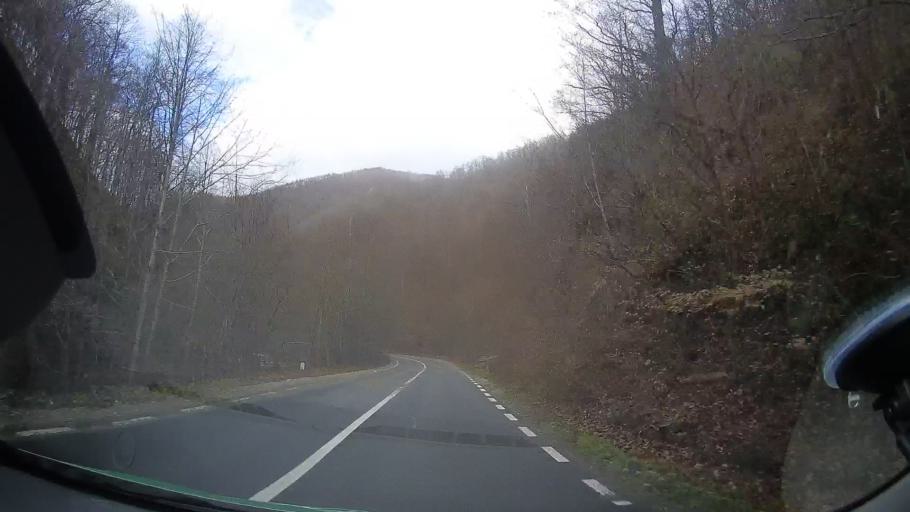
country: RO
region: Cluj
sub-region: Comuna Valea Ierii
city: Valea Ierii
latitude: 46.6276
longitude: 23.3871
